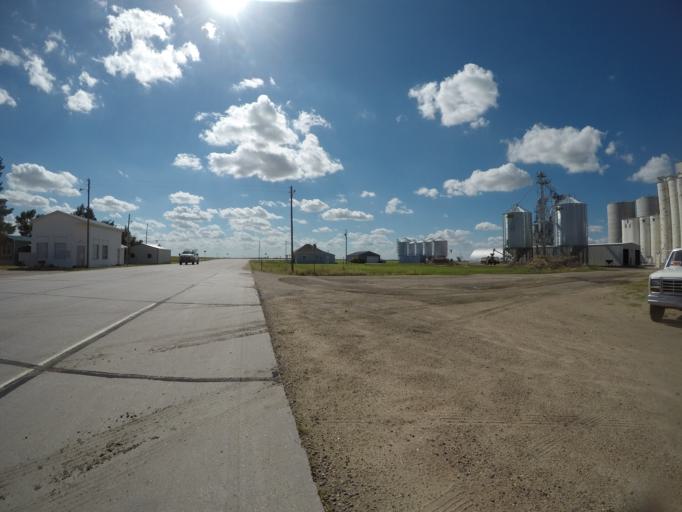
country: US
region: Colorado
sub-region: Phillips County
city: Holyoke
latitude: 40.6117
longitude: -102.4736
